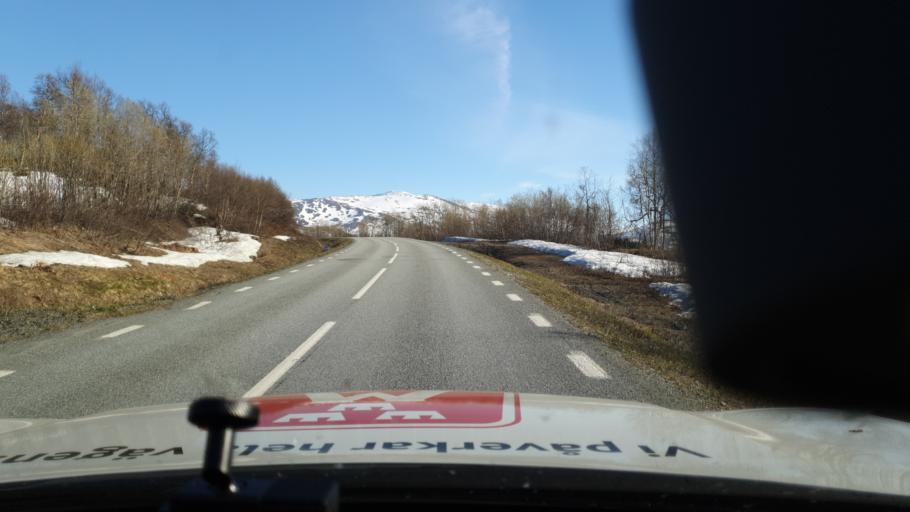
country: NO
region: Nordland
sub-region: Rana
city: Mo i Rana
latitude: 66.0873
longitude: 14.8588
